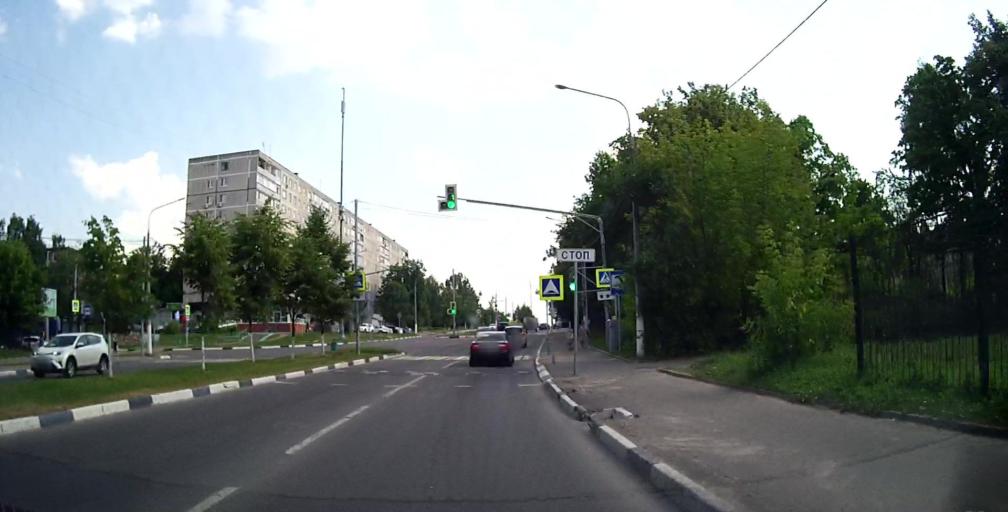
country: RU
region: Moskovskaya
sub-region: Podol'skiy Rayon
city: Podol'sk
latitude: 55.4190
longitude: 37.5192
